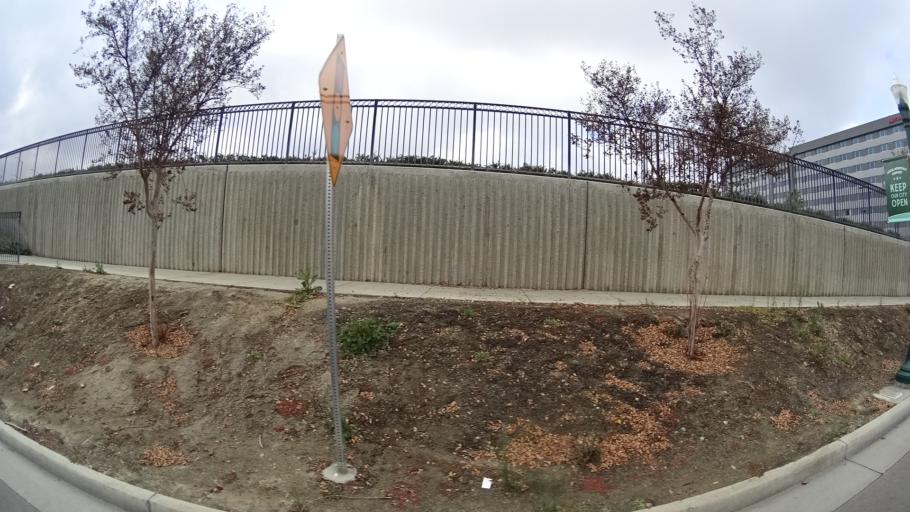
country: US
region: California
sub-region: Kern County
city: Bakersfield
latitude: 35.3720
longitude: -119.0107
